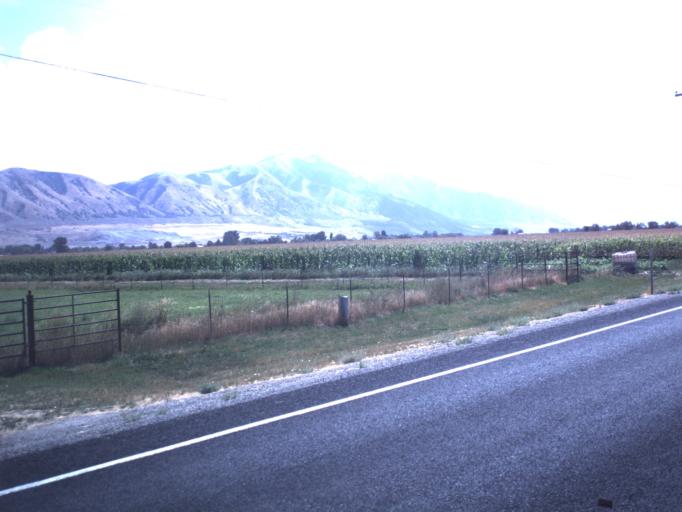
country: US
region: Utah
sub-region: Box Elder County
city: Garland
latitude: 41.7807
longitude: -112.1493
